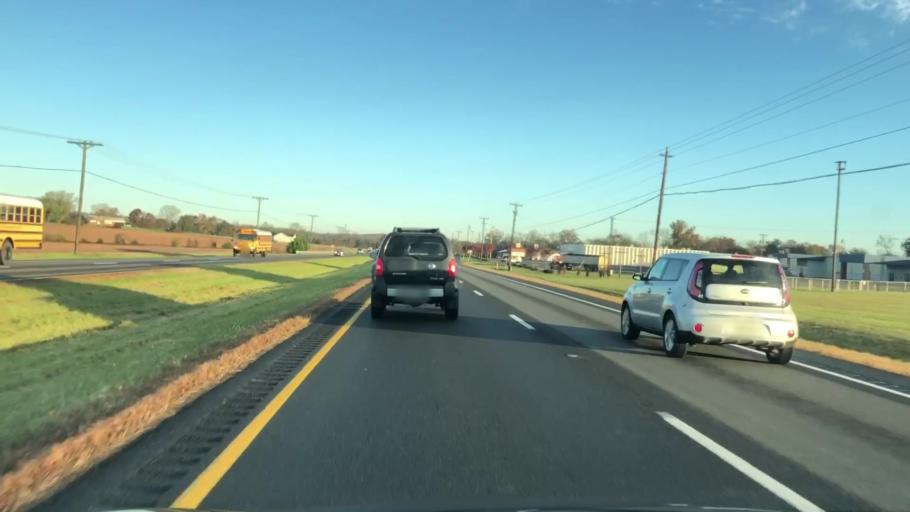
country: US
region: Virginia
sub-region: Fauquier County
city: Bealeton
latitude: 38.5344
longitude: -77.7291
